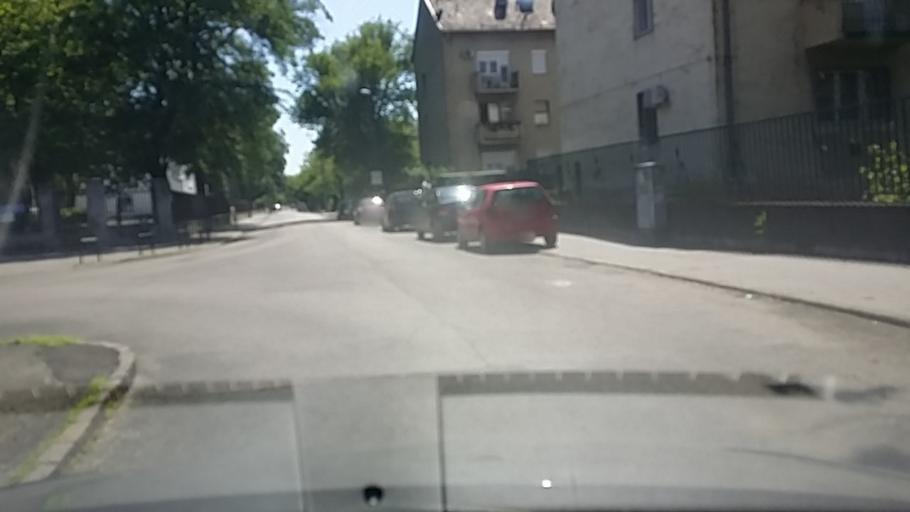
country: HU
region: Budapest
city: Budapest XV. keruelet
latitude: 47.5391
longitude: 19.1218
